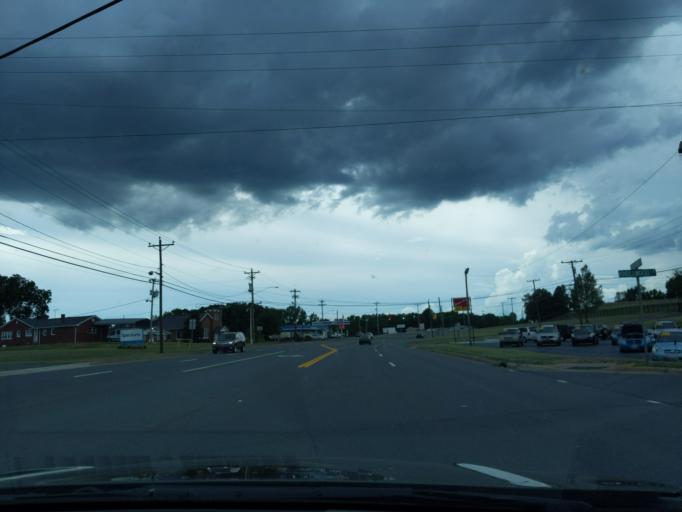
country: US
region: North Carolina
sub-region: Stanly County
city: Albemarle
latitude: 35.3970
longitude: -80.2003
